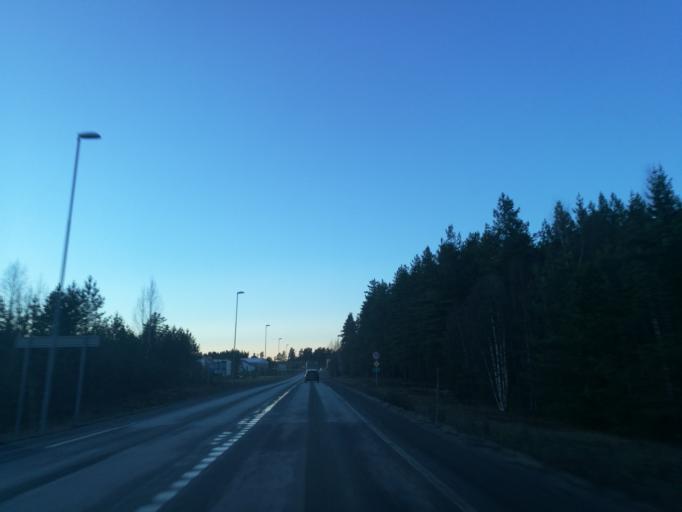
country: SE
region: Vaermland
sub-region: Eda Kommun
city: Charlottenberg
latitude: 59.9343
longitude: 12.2280
